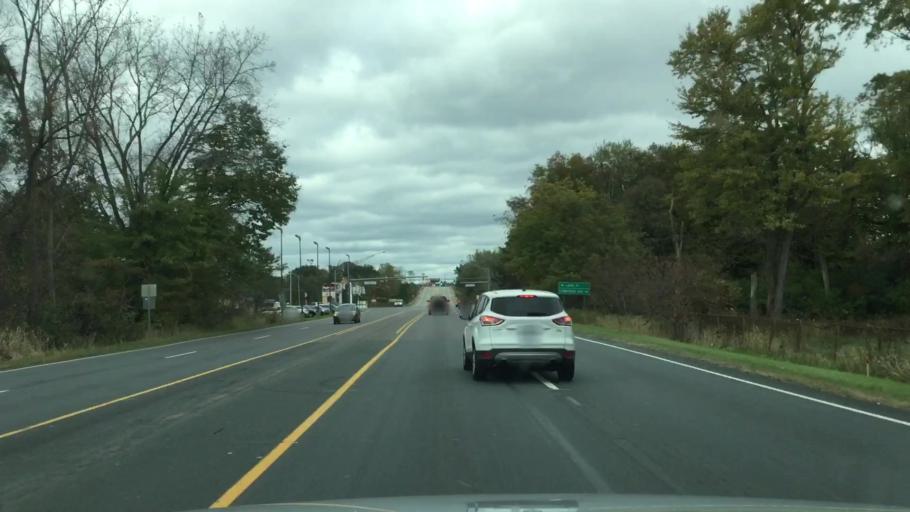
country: US
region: Michigan
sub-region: Kalamazoo County
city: Eastwood
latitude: 42.2812
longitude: -85.5307
